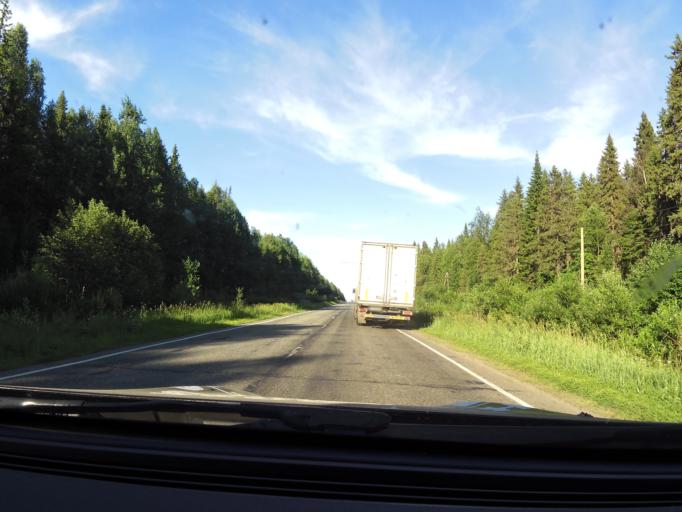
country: RU
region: Kirov
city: Belorechensk
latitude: 58.8020
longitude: 52.4200
